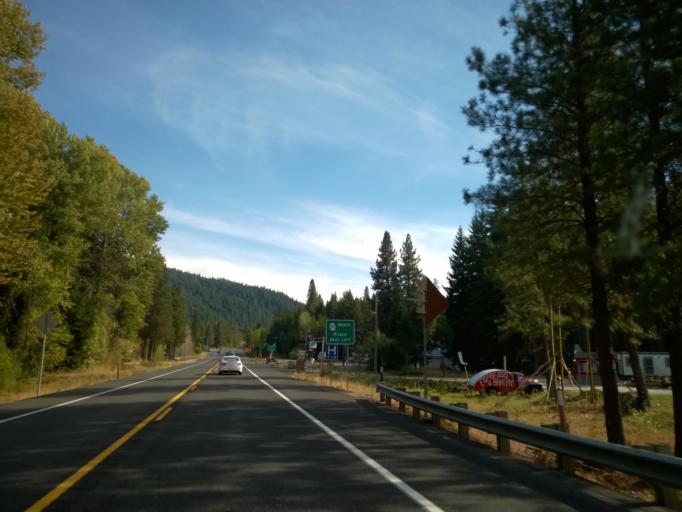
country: US
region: Washington
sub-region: Chelan County
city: Leavenworth
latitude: 47.7596
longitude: -120.7419
